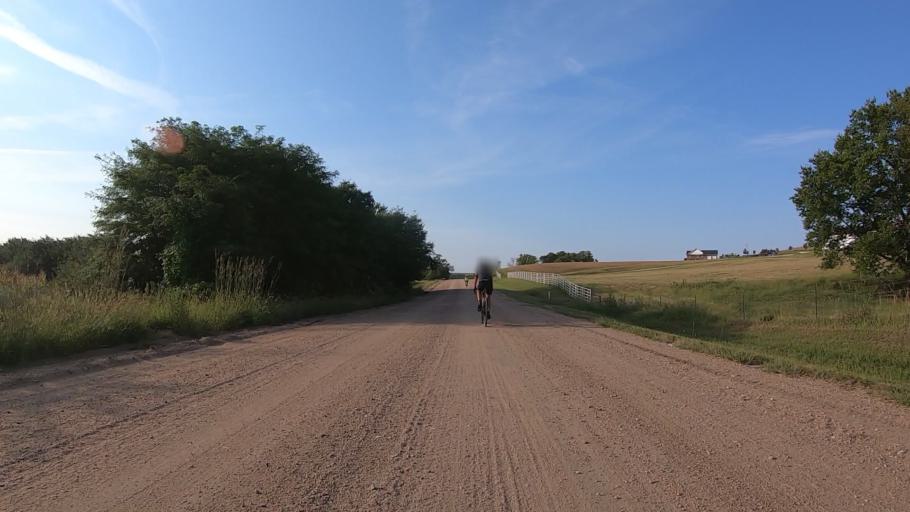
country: US
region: Kansas
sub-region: Marshall County
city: Blue Rapids
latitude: 39.6847
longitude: -96.7790
